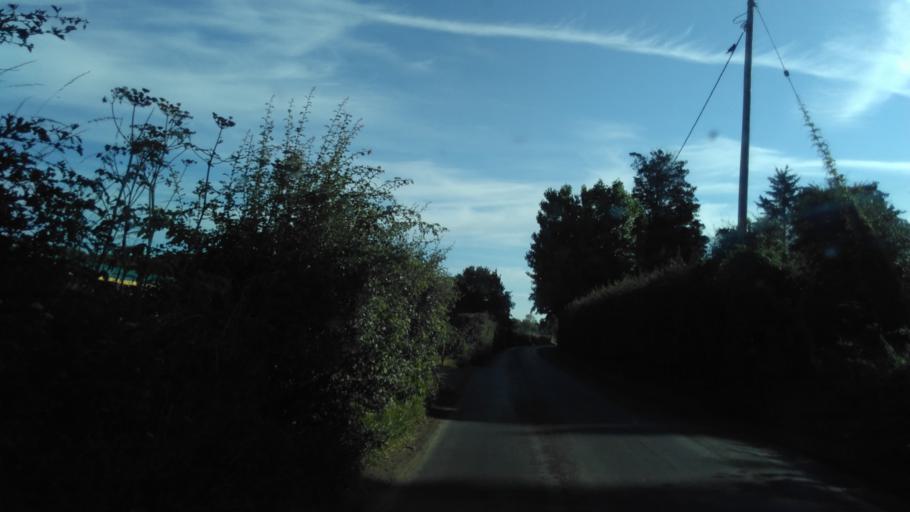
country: GB
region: England
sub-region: Kent
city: Faversham
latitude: 51.3164
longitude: 0.9363
